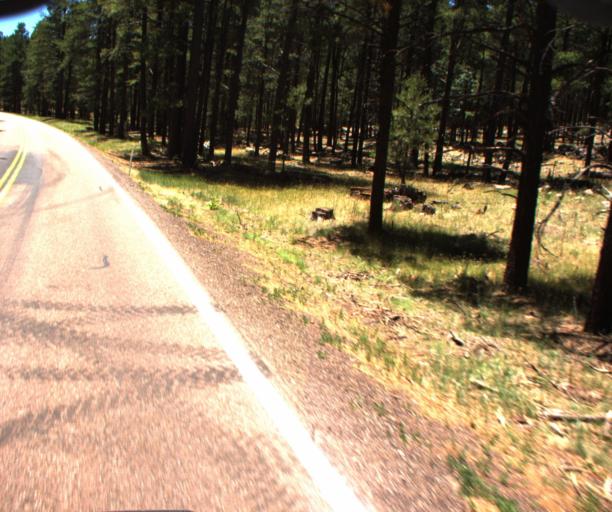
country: US
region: Arizona
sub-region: Gila County
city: Pine
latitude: 34.5342
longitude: -111.3396
